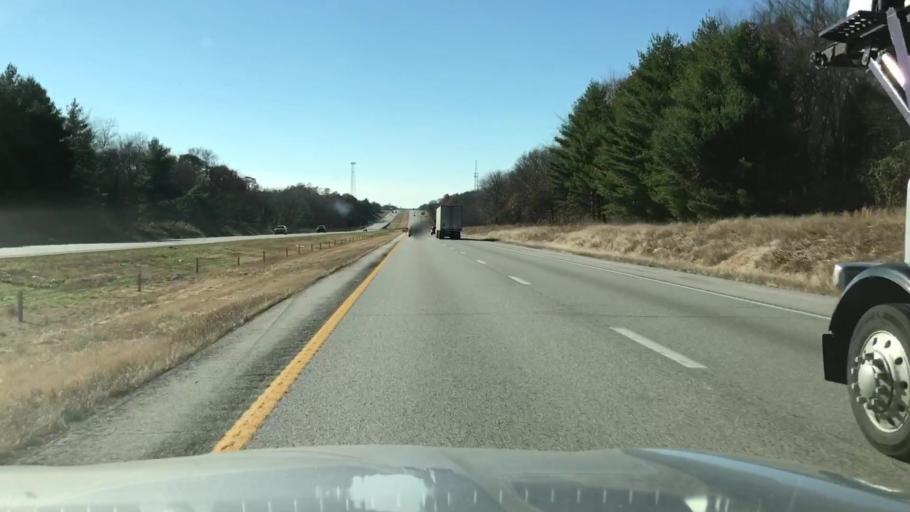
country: US
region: Missouri
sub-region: Jasper County
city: Duenweg
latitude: 37.0802
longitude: -94.3717
